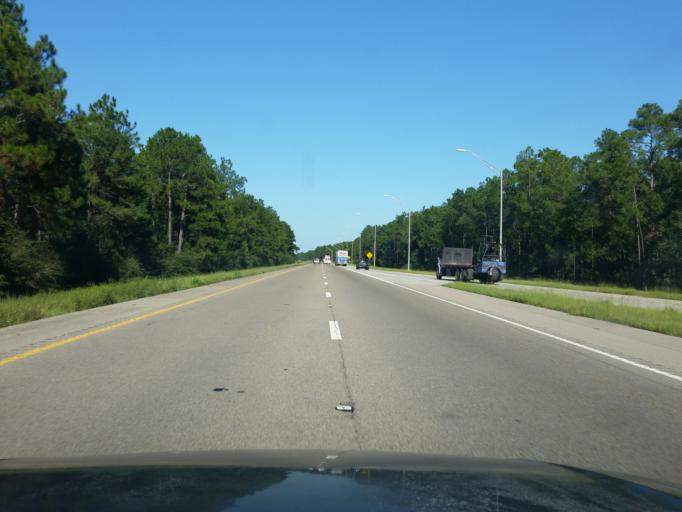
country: US
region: Mississippi
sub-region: Hancock County
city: Kiln
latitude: 30.3453
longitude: -89.4662
